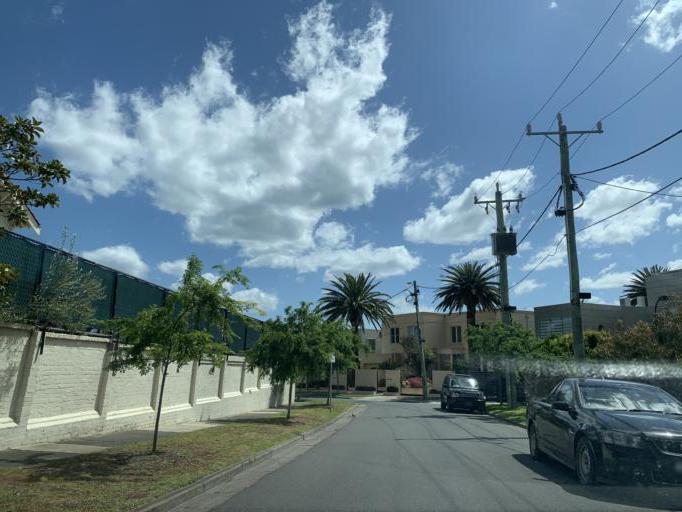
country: AU
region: Victoria
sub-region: Port Phillip
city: Elwood
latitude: -37.9017
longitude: 144.9853
